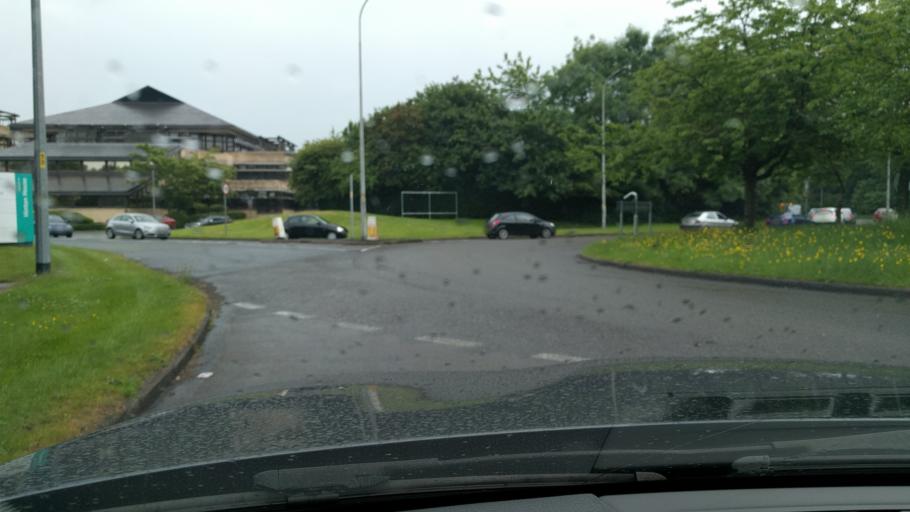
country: GB
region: England
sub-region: Warrington
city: Croft
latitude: 53.4269
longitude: -2.5334
